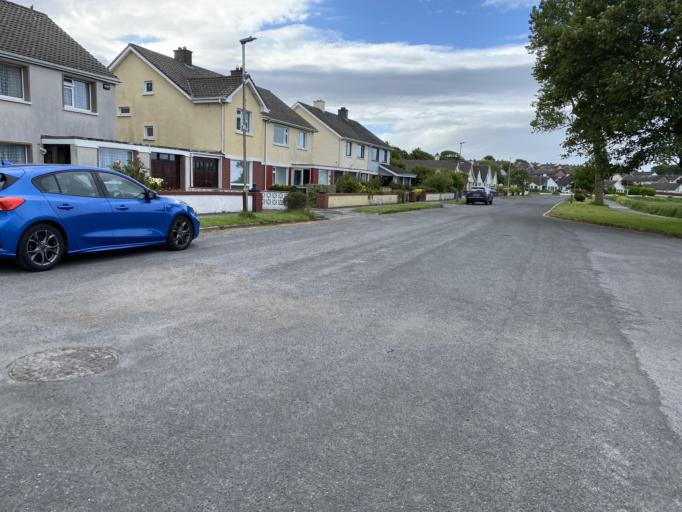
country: IE
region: Connaught
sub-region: County Galway
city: Gaillimh
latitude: 53.2785
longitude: -9.0294
